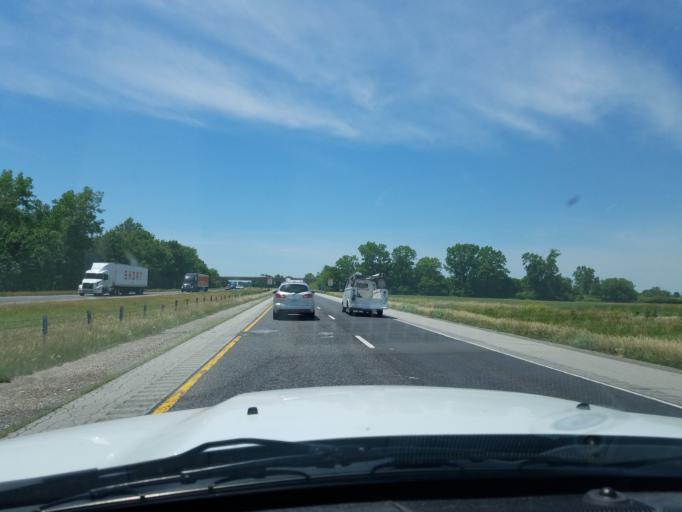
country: US
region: Indiana
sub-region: Madison County
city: Pendleton
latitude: 40.0312
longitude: -85.7457
